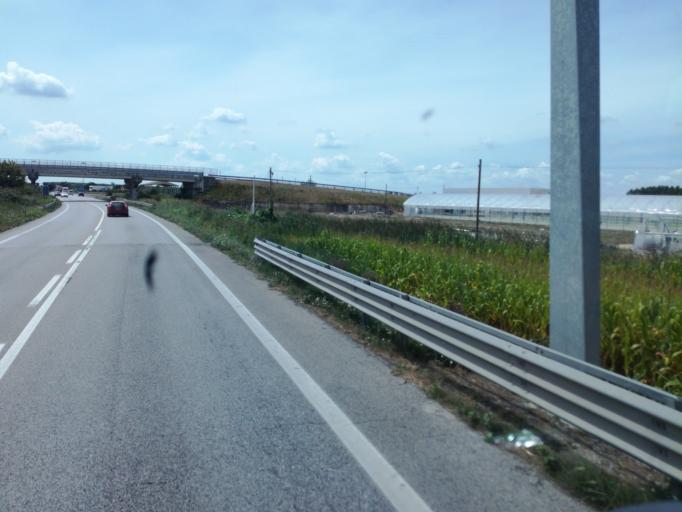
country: IT
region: Veneto
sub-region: Provincia di Rovigo
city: Taglio di Po
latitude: 44.9804
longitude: 12.2208
